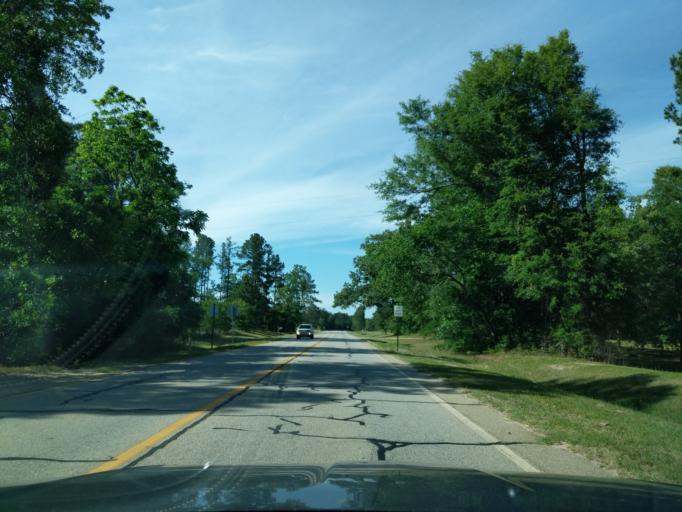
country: US
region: Georgia
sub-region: Jefferson County
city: Wrens
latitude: 33.2491
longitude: -82.3872
